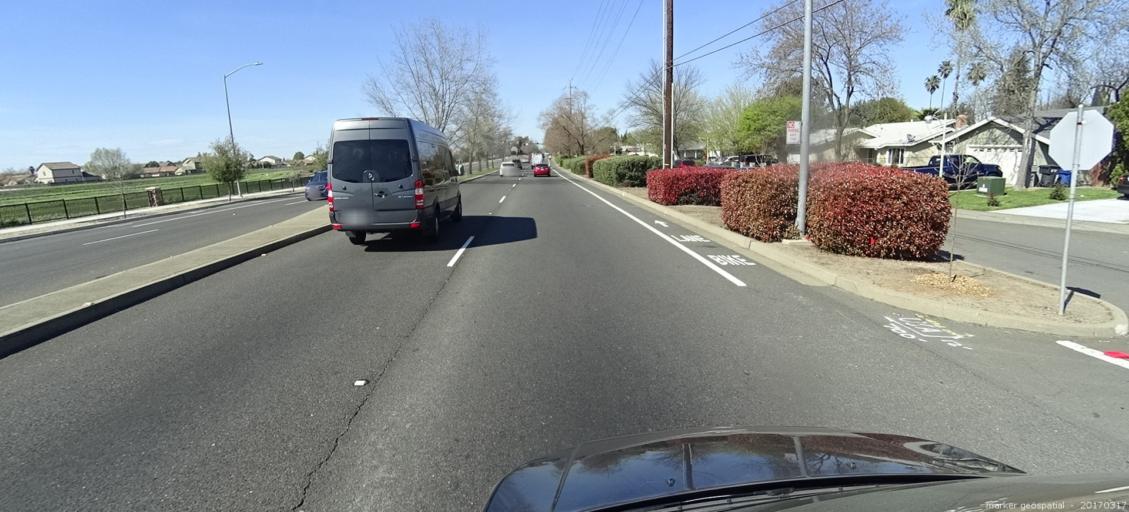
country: US
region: California
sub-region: Sacramento County
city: Parkway
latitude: 38.4762
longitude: -121.4510
